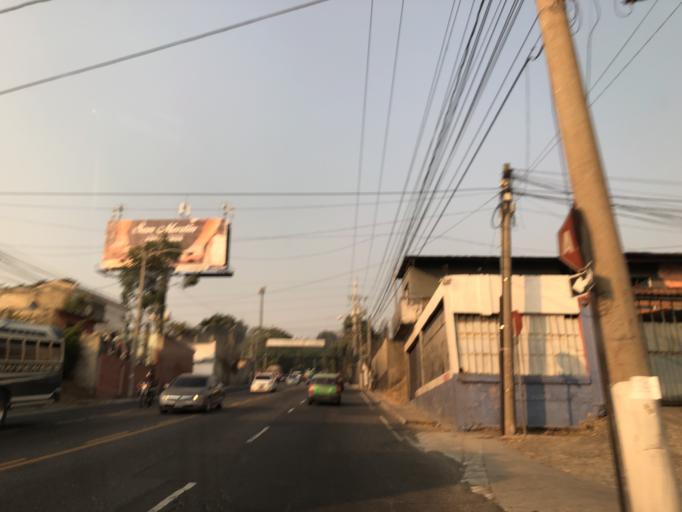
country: GT
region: Guatemala
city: Santa Catarina Pinula
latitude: 14.5649
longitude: -90.5286
